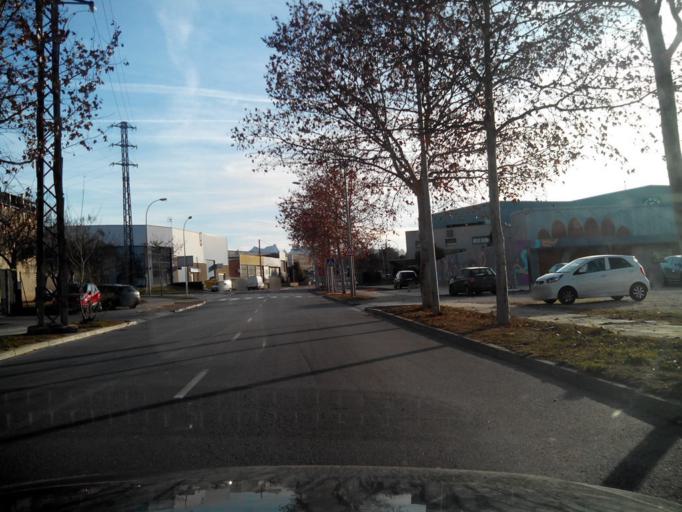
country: ES
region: Catalonia
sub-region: Provincia de Barcelona
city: Manresa
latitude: 41.7163
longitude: 1.8458
